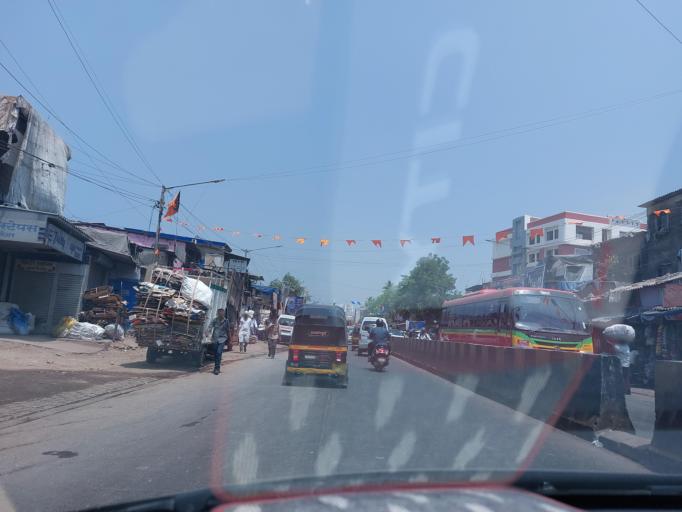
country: IN
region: Maharashtra
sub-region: Mumbai Suburban
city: Mumbai
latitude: 19.0577
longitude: 72.8867
